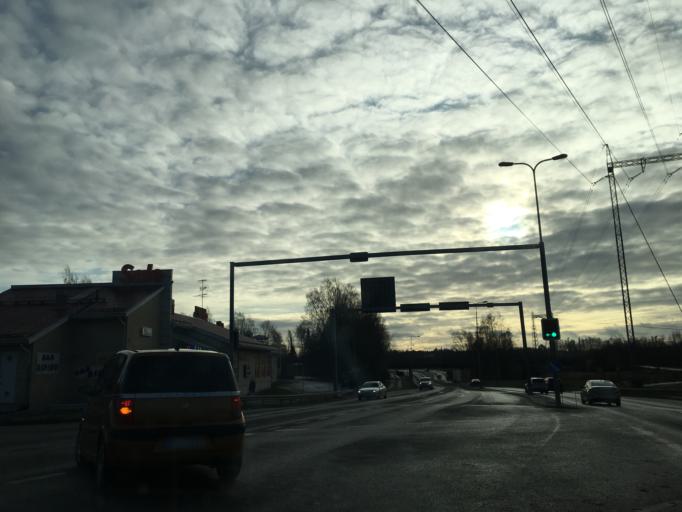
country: FI
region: Varsinais-Suomi
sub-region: Turku
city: Raisio
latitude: 60.4601
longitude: 22.1963
